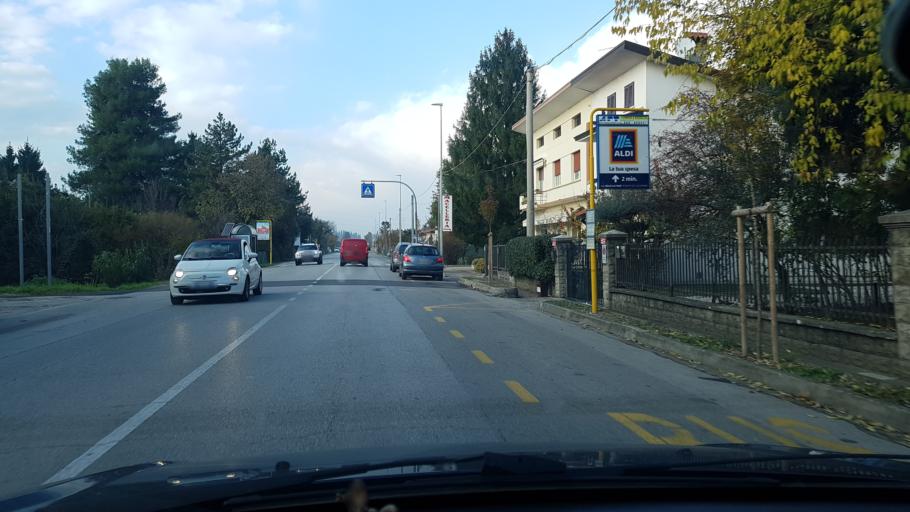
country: IT
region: Friuli Venezia Giulia
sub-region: Provincia di Gorizia
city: Ronchi dei Legionari
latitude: 45.8359
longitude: 13.4964
